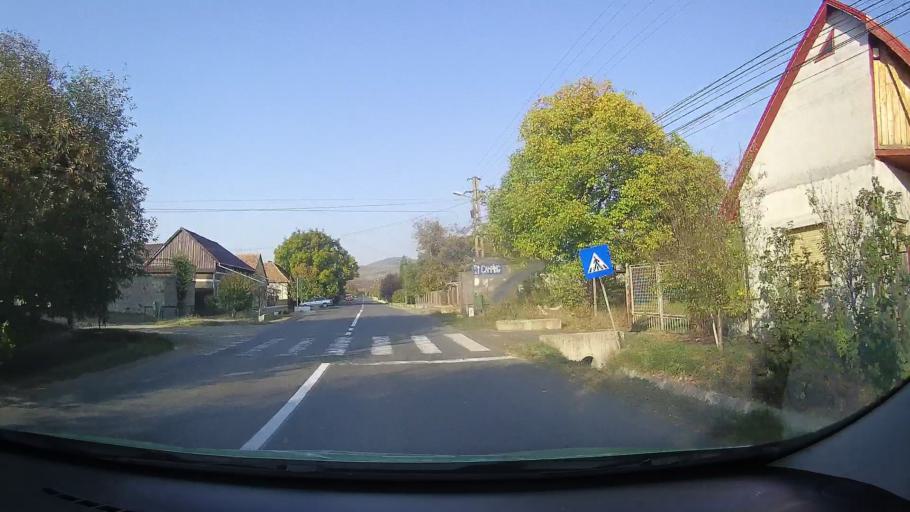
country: RO
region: Arad
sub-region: Comuna Paulis
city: Paulis
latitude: 46.1312
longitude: 21.6018
